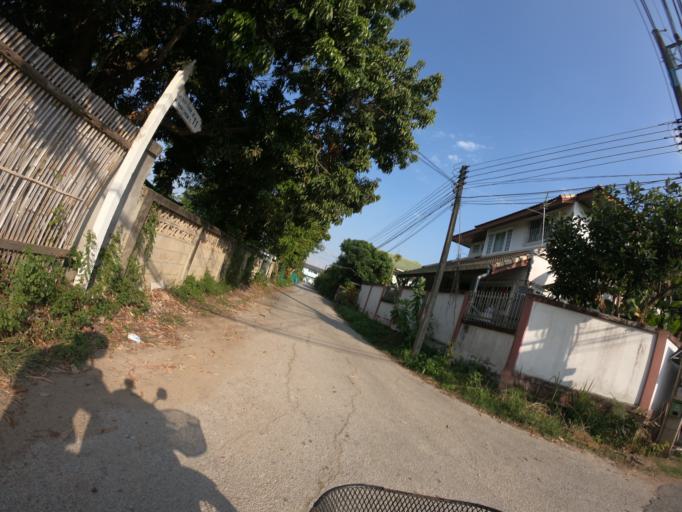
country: TH
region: Chiang Mai
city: Chiang Mai
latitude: 18.8309
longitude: 98.9886
